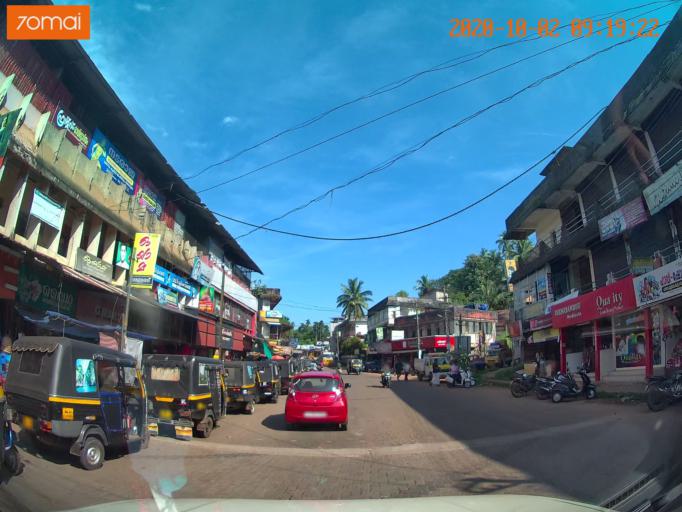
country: IN
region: Kerala
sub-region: Kozhikode
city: Naduvannur
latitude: 11.5626
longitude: 75.7572
